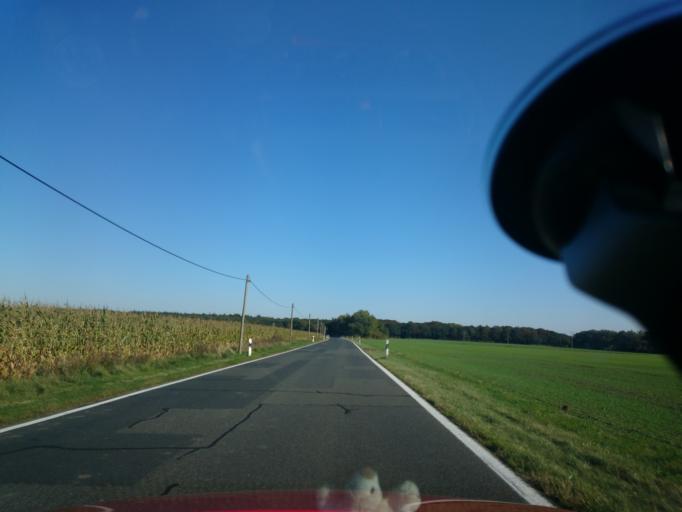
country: DE
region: Mecklenburg-Vorpommern
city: Saal
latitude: 54.3351
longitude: 12.5390
